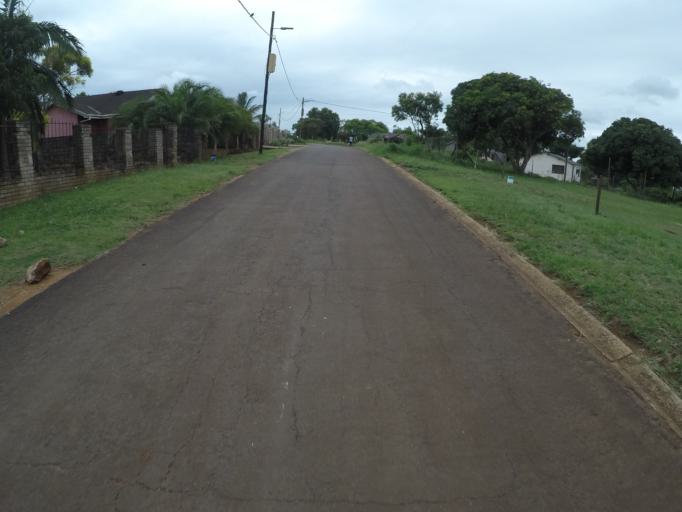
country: ZA
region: KwaZulu-Natal
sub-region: uThungulu District Municipality
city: Empangeni
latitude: -28.7702
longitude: 31.8691
